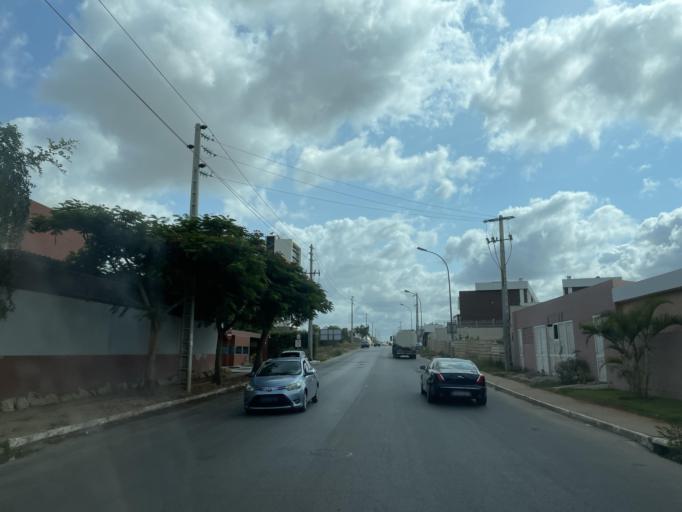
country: AO
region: Luanda
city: Luanda
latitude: -8.9227
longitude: 13.1999
